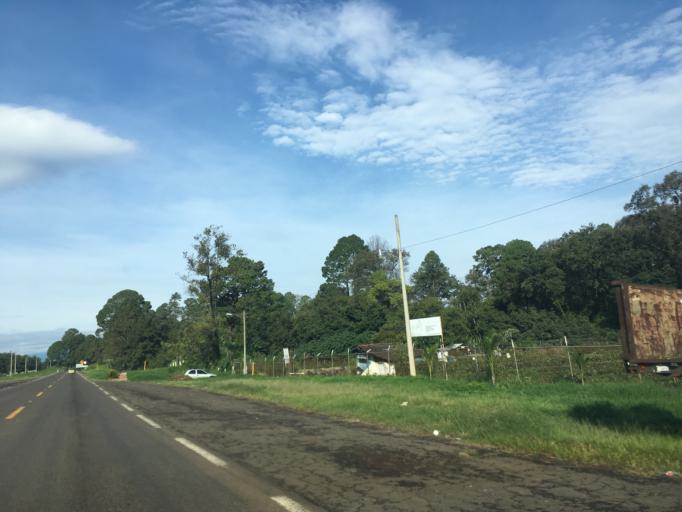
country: MX
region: Michoacan
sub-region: Uruapan
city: Toreo Bajo (El Toreo Bajo)
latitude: 19.4535
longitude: -101.9798
